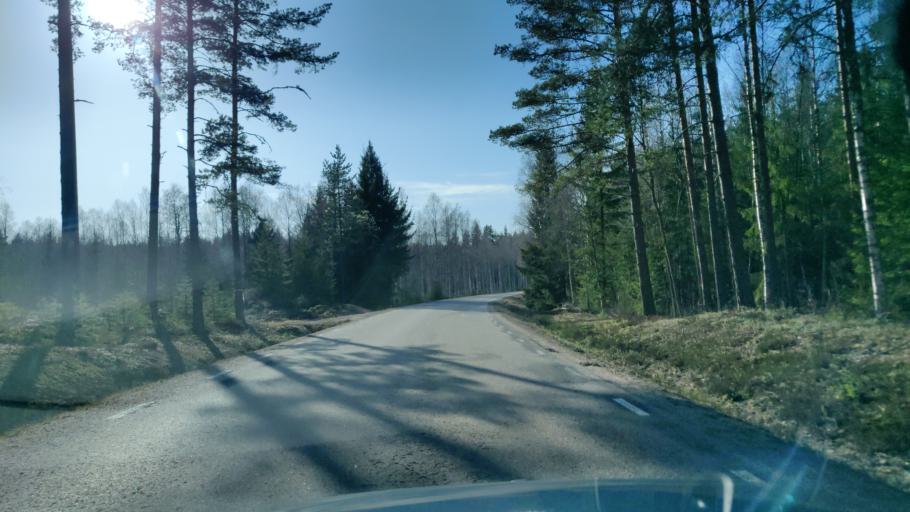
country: SE
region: Vaermland
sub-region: Sunne Kommun
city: Sunne
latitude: 59.9856
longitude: 13.3206
